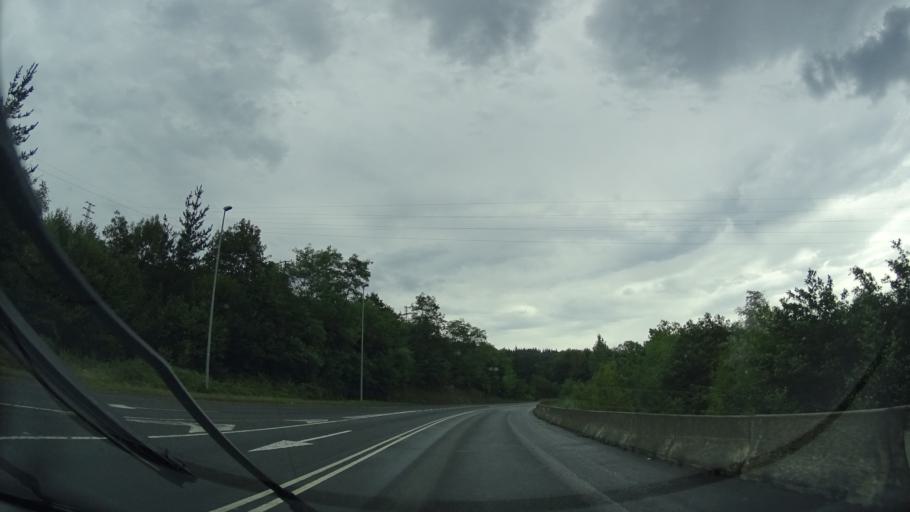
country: ES
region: Basque Country
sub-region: Bizkaia
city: Amorebieta
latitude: 43.1897
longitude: -2.7758
